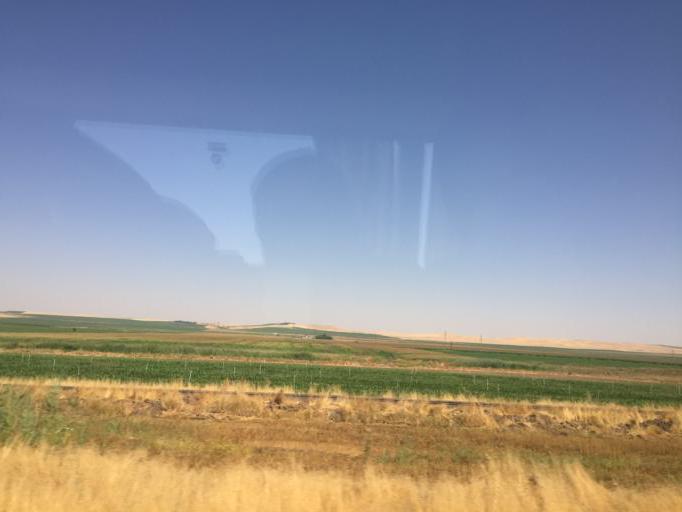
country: TR
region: Diyarbakir
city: Tepe
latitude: 37.8501
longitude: 40.7800
